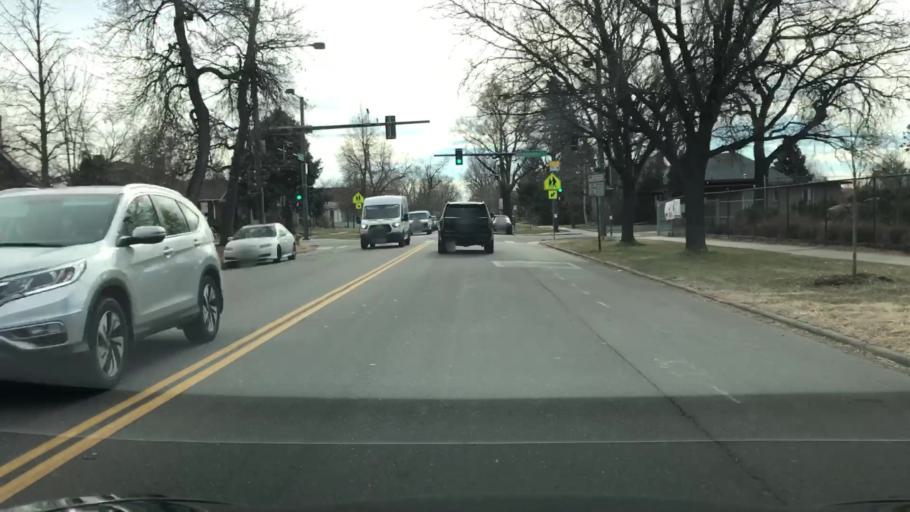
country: US
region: Colorado
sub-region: Denver County
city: Denver
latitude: 39.6935
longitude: -104.9828
